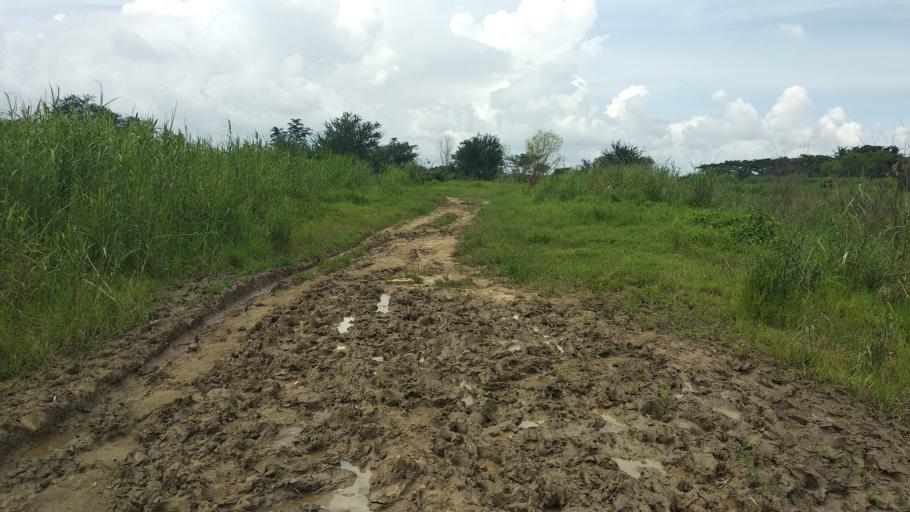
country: MM
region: Yangon
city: Kanbe
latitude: 16.8788
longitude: 95.9751
